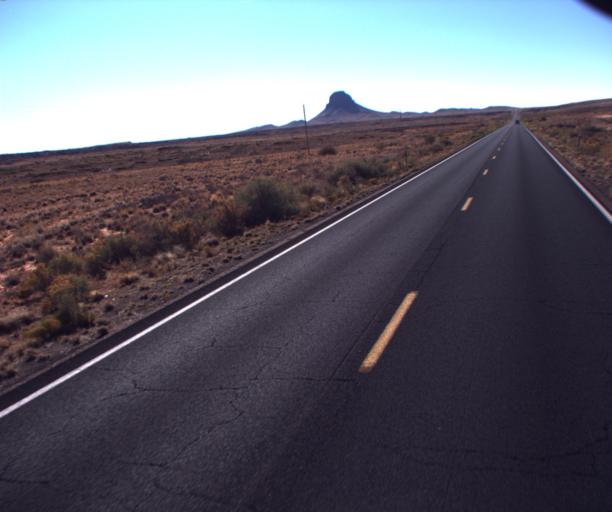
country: US
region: Arizona
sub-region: Navajo County
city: Dilkon
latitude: 35.3374
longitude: -110.4238
